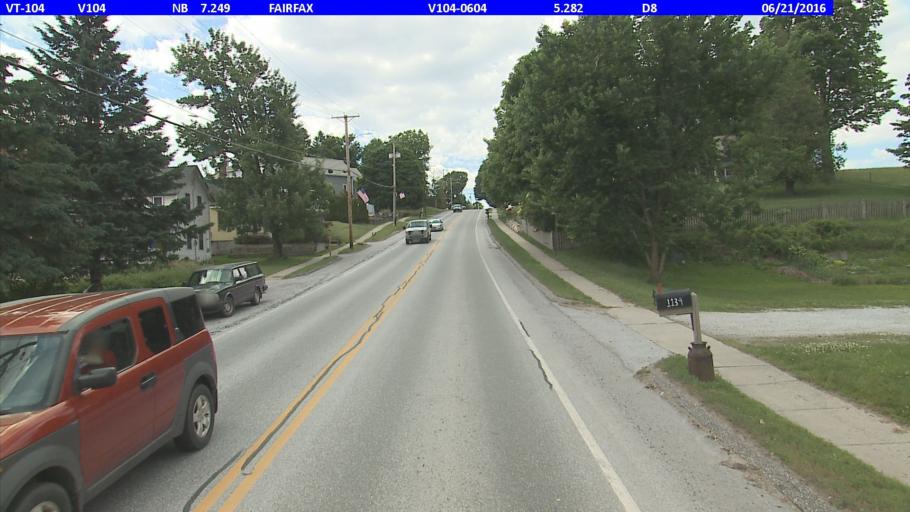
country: US
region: Vermont
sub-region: Chittenden County
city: Milton
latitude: 44.6661
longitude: -73.0099
